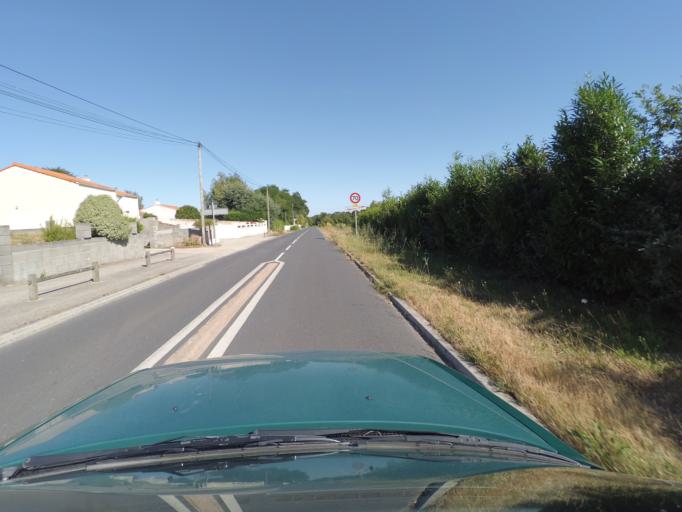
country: FR
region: Pays de la Loire
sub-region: Departement de la Loire-Atlantique
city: Maisdon-sur-Sevre
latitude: 47.0938
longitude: -1.3755
